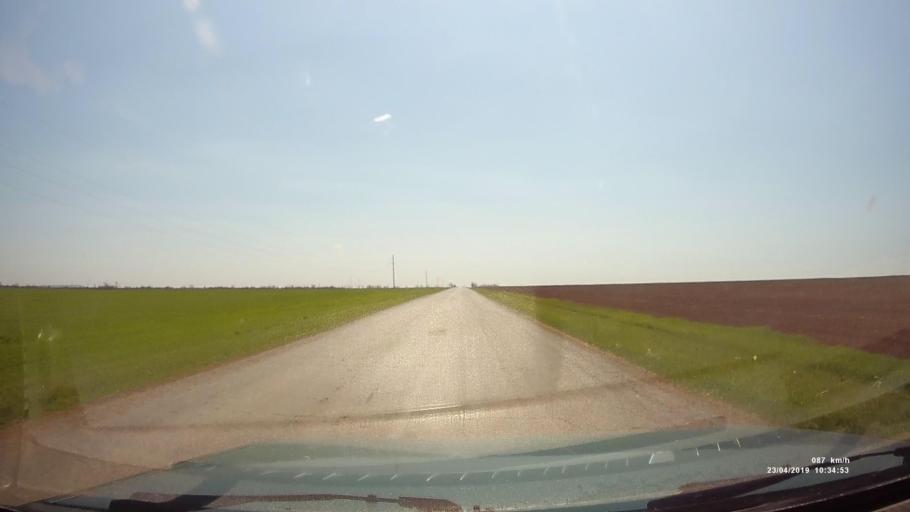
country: RU
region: Kalmykiya
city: Yashalta
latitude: 46.5597
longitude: 42.6162
